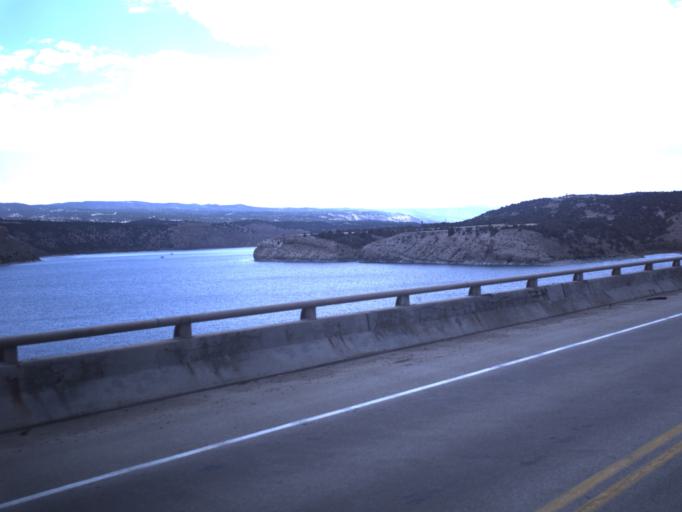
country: US
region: Utah
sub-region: Duchesne County
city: Duchesne
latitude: 40.1732
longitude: -110.4946
